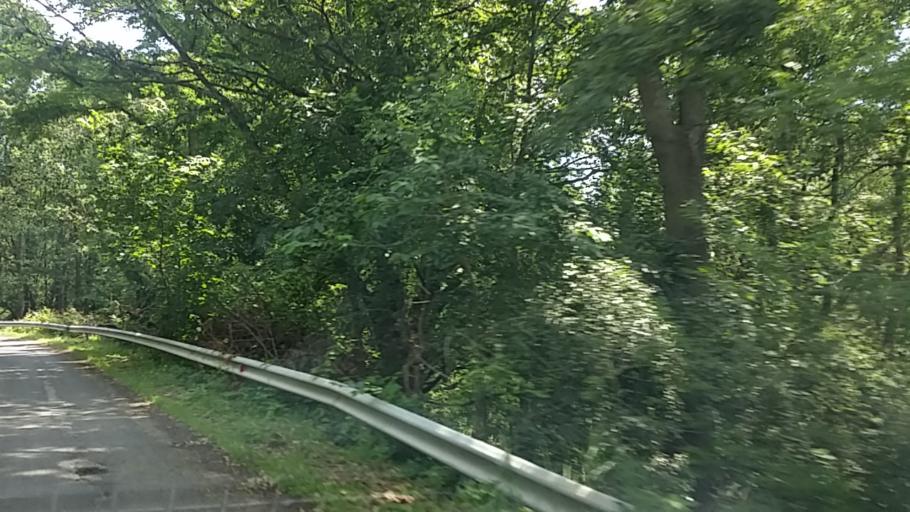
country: HU
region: Nograd
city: Batonyterenye
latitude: 47.9042
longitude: 19.8459
